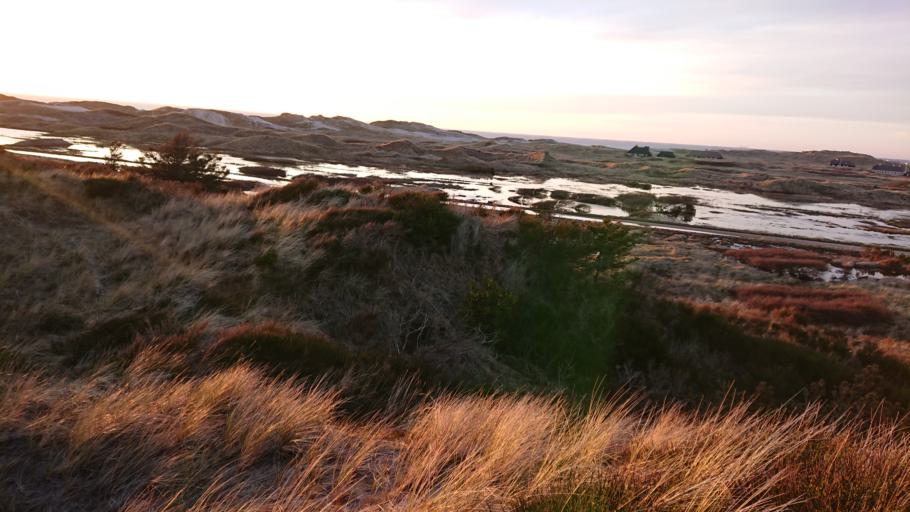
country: DK
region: North Denmark
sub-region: Frederikshavn Kommune
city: Skagen
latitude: 57.7190
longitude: 10.5146
